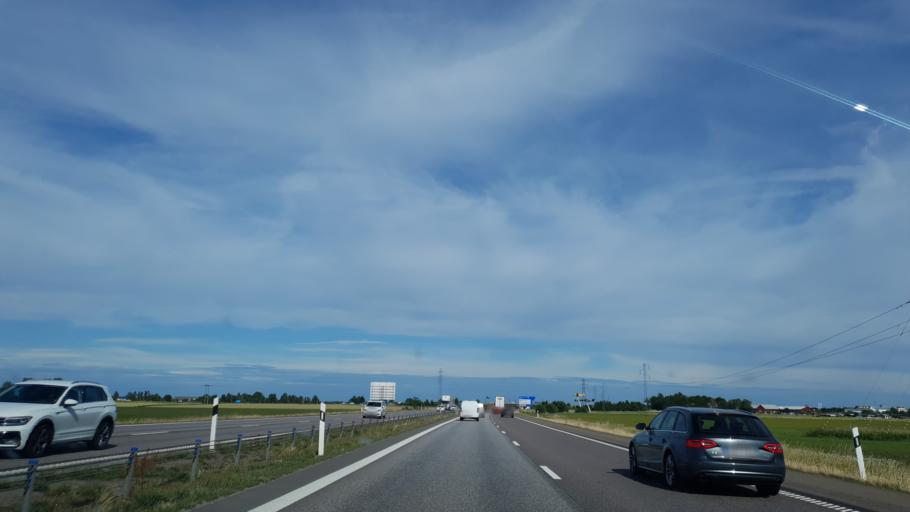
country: SE
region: OEstergoetland
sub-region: Linkopings Kommun
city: Malmslatt
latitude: 58.4387
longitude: 15.5658
